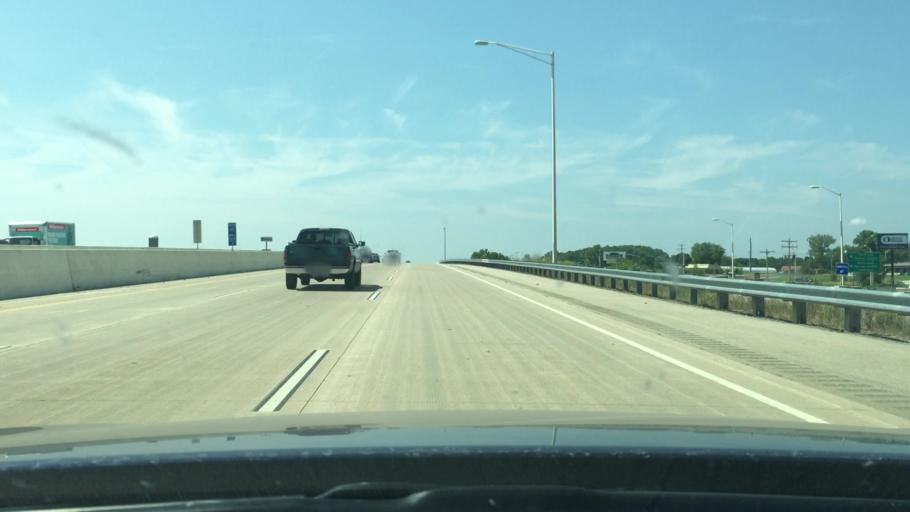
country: US
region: Wisconsin
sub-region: Winnebago County
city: Oshkosh
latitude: 44.0990
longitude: -88.5406
